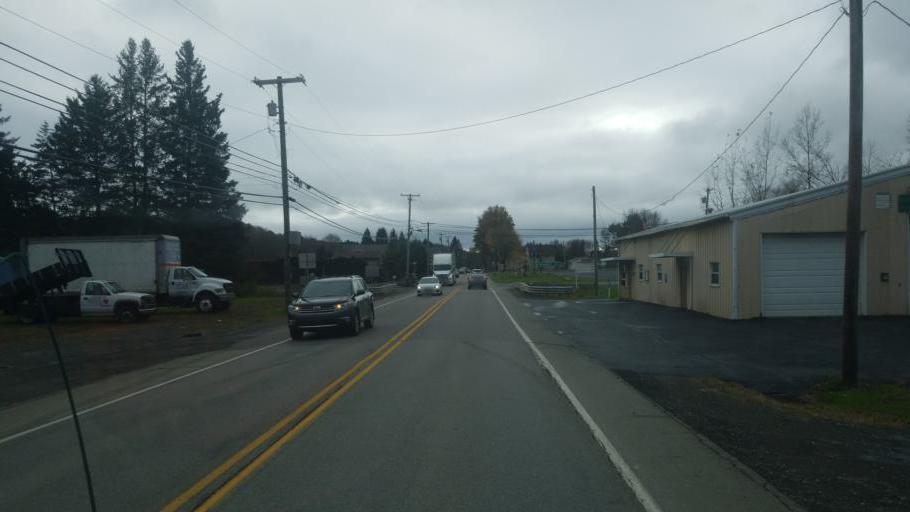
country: US
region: Pennsylvania
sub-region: Jefferson County
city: Brockway
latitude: 41.2610
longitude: -78.7252
